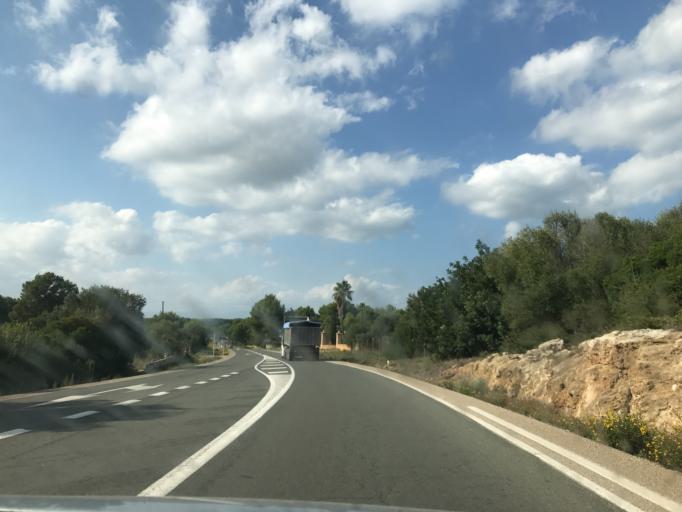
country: ES
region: Balearic Islands
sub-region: Illes Balears
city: Santa Margalida
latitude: 39.7239
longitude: 3.2095
